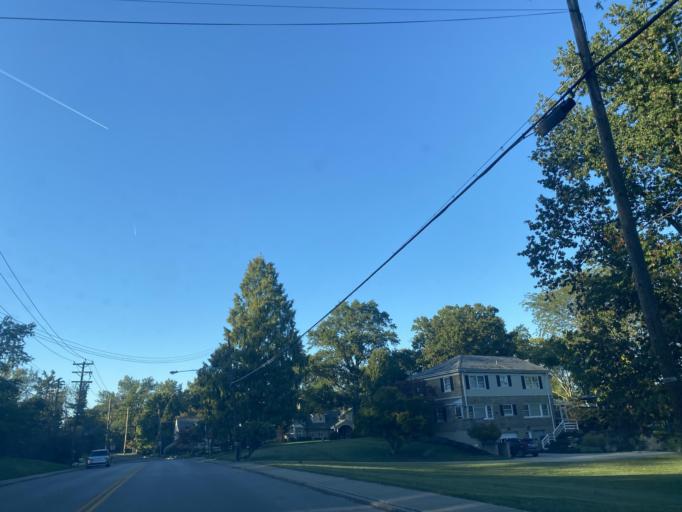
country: US
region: Kentucky
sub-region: Campbell County
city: Fort Thomas
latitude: 39.1009
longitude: -84.4496
